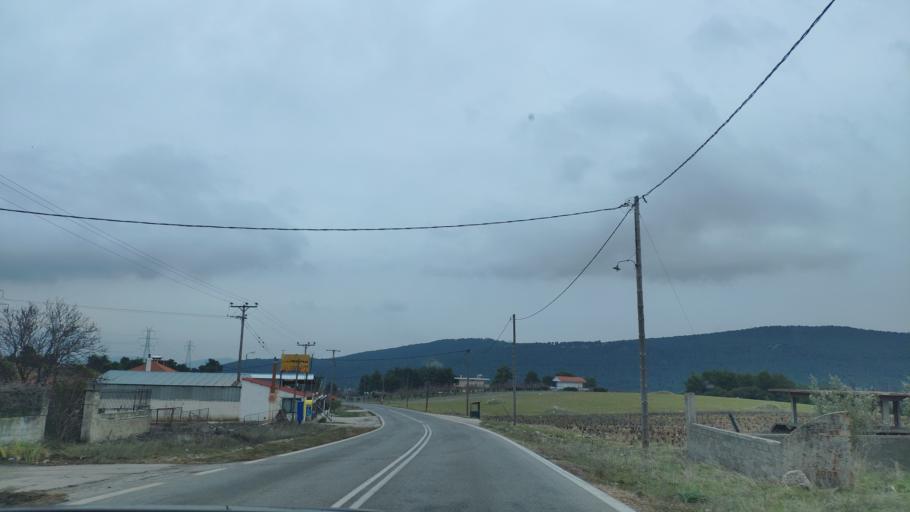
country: GR
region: Attica
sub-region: Nomarchia Dytikis Attikis
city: Vilia
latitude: 38.1735
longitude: 23.3853
